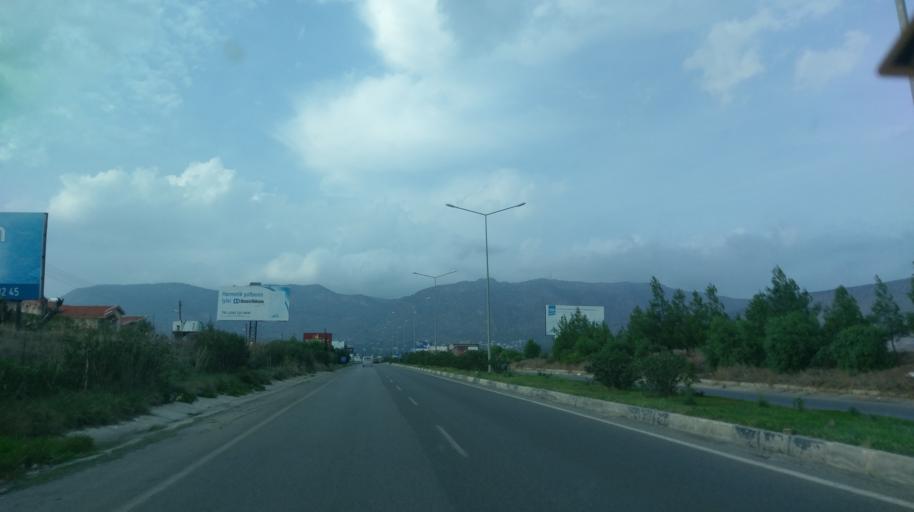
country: CY
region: Keryneia
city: Kyrenia
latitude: 35.2692
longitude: 33.2907
